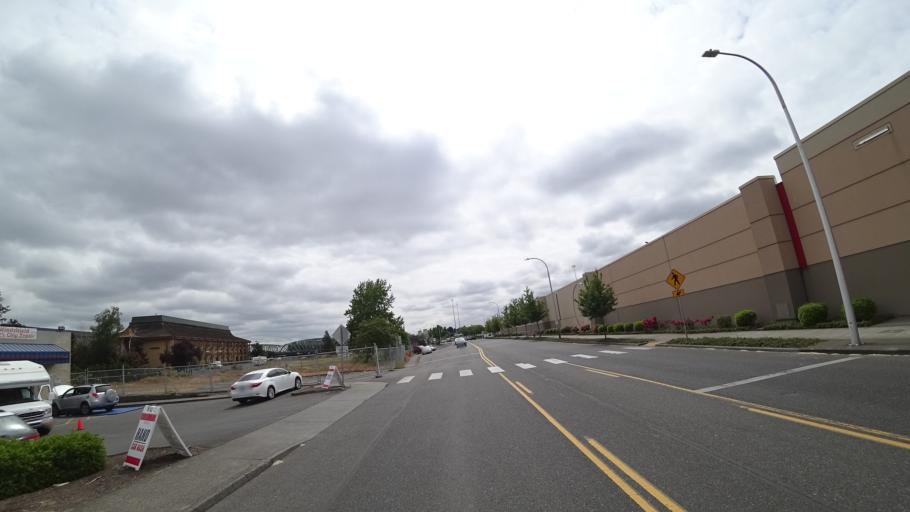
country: US
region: Washington
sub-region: Clark County
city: Vancouver
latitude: 45.6143
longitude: -122.6829
